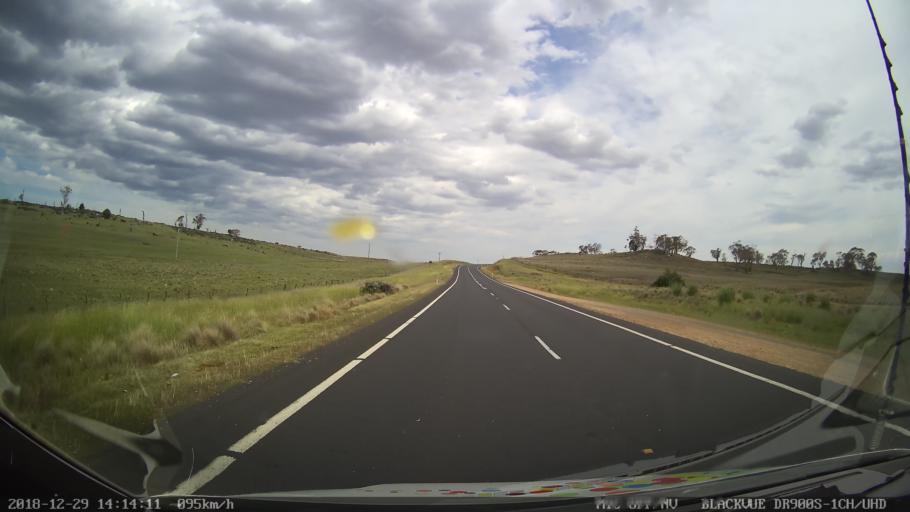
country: AU
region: New South Wales
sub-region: Cooma-Monaro
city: Cooma
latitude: -36.4391
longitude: 149.2374
